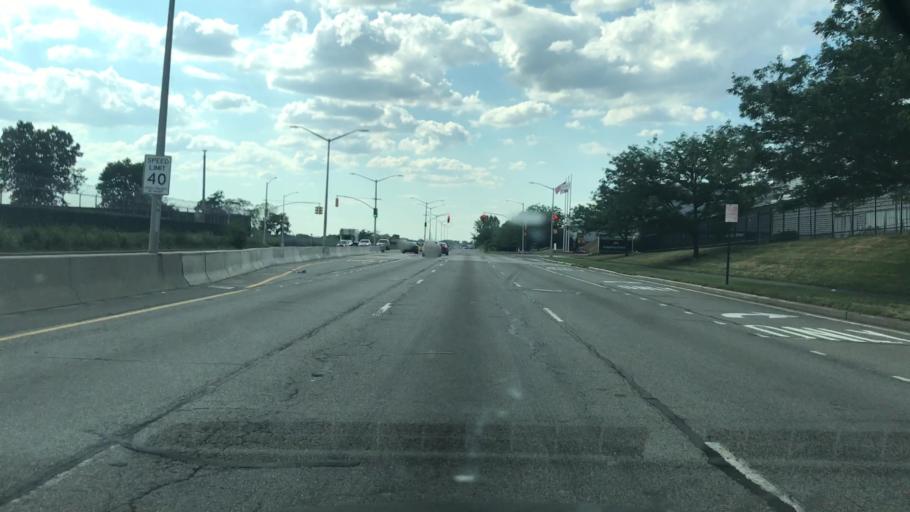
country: US
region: New York
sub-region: Nassau County
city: Inwood
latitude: 40.6500
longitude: -73.7563
